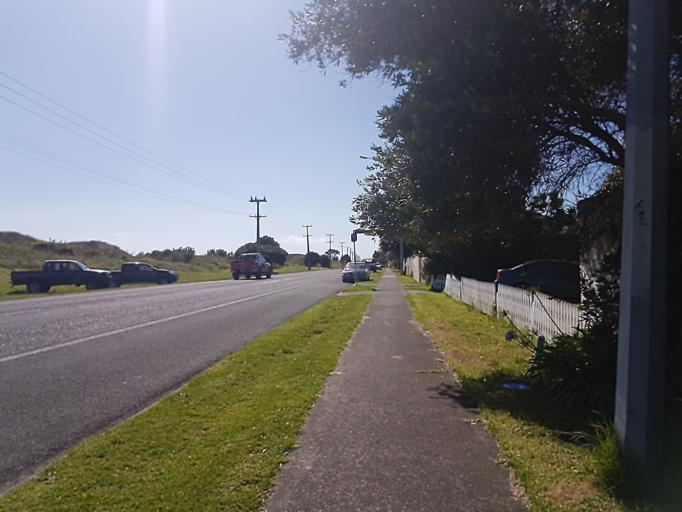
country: NZ
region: Bay of Plenty
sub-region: Tauranga City
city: Tauranga
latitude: -37.7009
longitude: 176.2933
